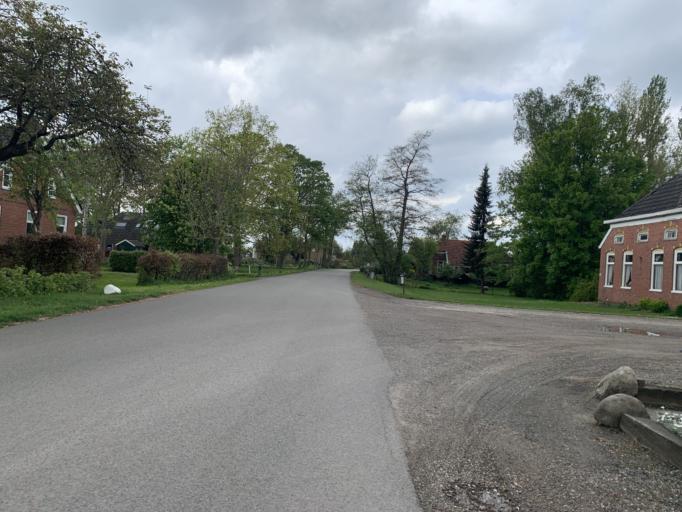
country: NL
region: Groningen
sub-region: Gemeente Haren
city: Haren
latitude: 53.2040
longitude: 6.6545
